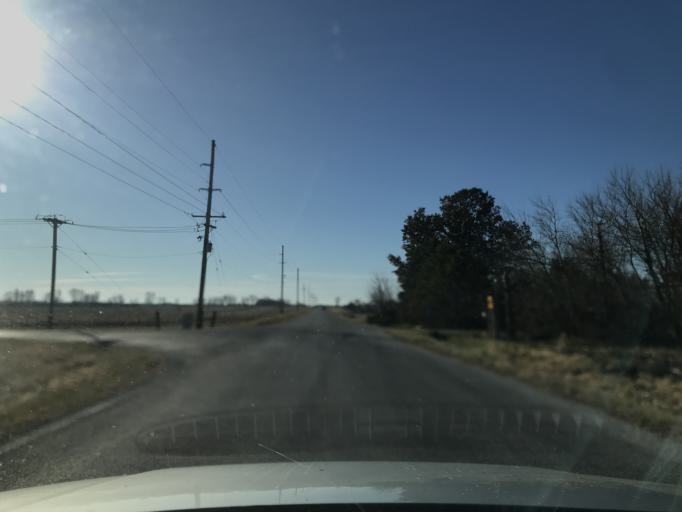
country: US
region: Illinois
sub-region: Hancock County
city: Carthage
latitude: 40.4692
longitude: -91.1783
